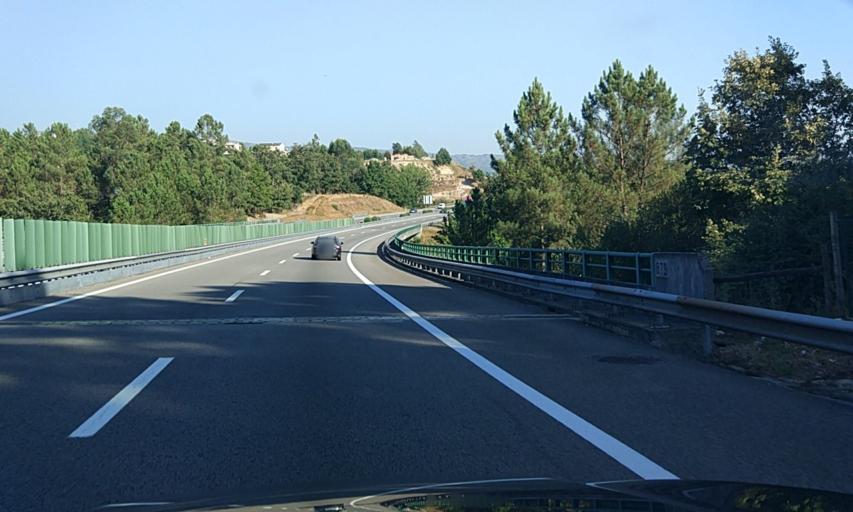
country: PT
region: Porto
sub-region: Marco de Canaveses
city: Marco de Canavezes
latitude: 41.2286
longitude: -8.1703
